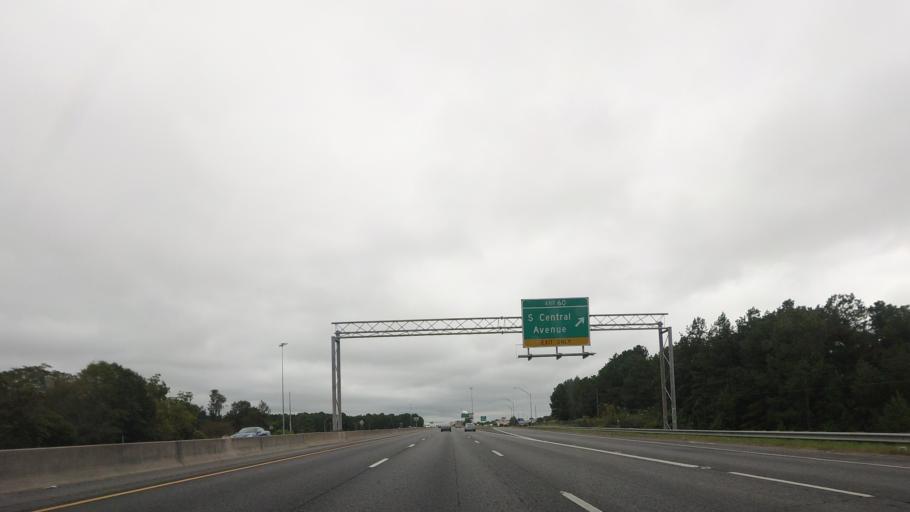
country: US
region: Georgia
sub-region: Tift County
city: Unionville
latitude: 31.4333
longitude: -83.5196
